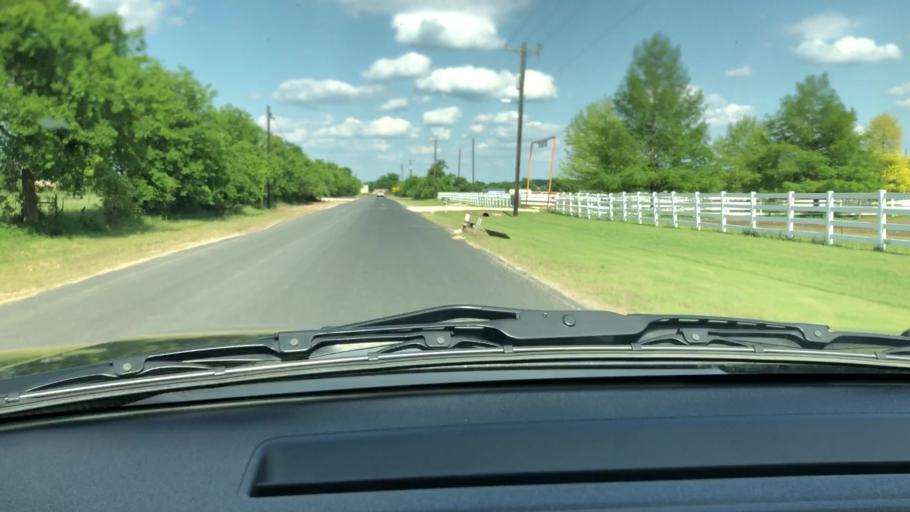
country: US
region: Texas
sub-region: Bexar County
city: Timberwood Park
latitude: 29.7307
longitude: -98.5019
